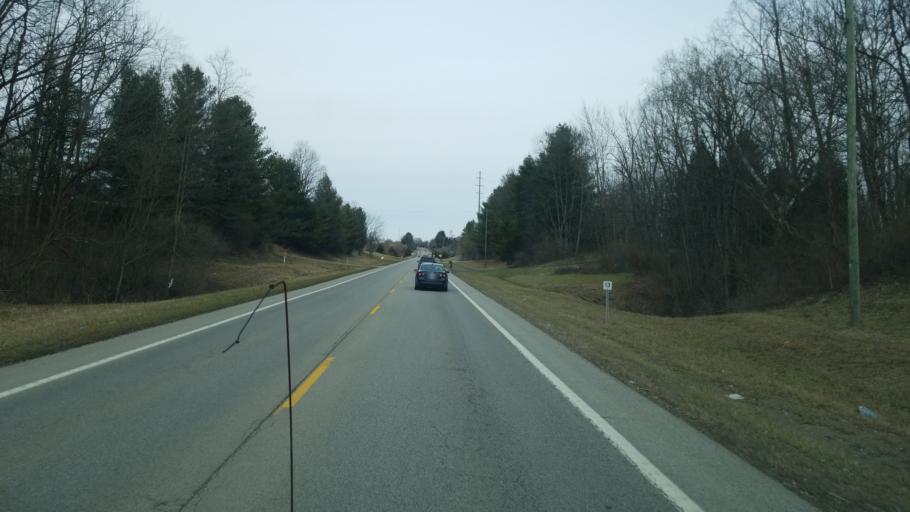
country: US
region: Ohio
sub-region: Highland County
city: Hillsboro
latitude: 39.1787
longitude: -83.6204
